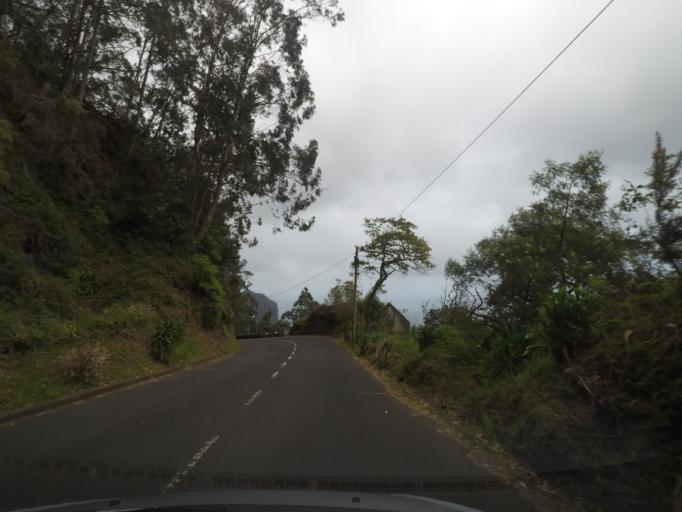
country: PT
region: Madeira
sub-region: Santa Cruz
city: Camacha
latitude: 32.7472
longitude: -16.8293
